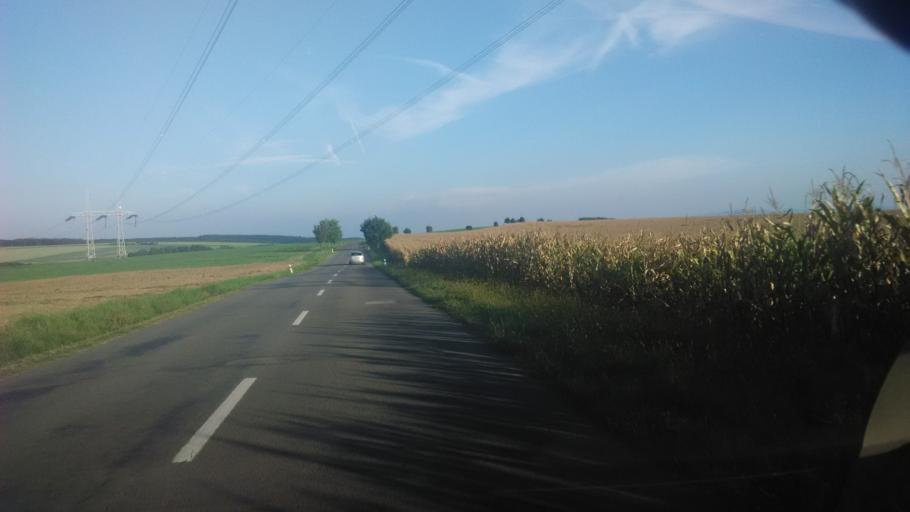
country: SK
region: Nitriansky
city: Levice
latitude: 48.2456
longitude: 18.7429
